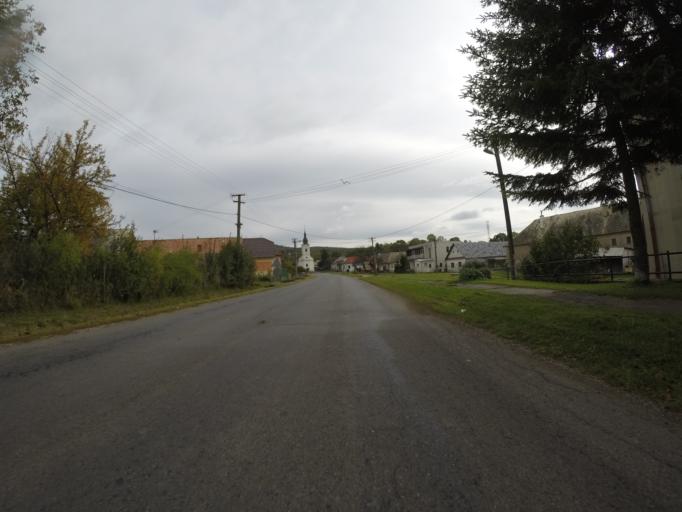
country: SK
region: Banskobystricky
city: Rimavska Sobota
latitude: 48.4701
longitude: 20.0993
